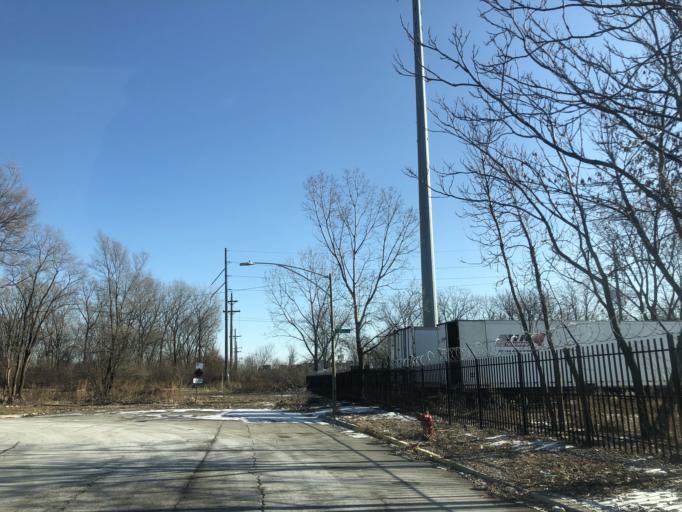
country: US
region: Illinois
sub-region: Cook County
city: Evergreen Park
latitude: 41.7593
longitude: -87.6798
